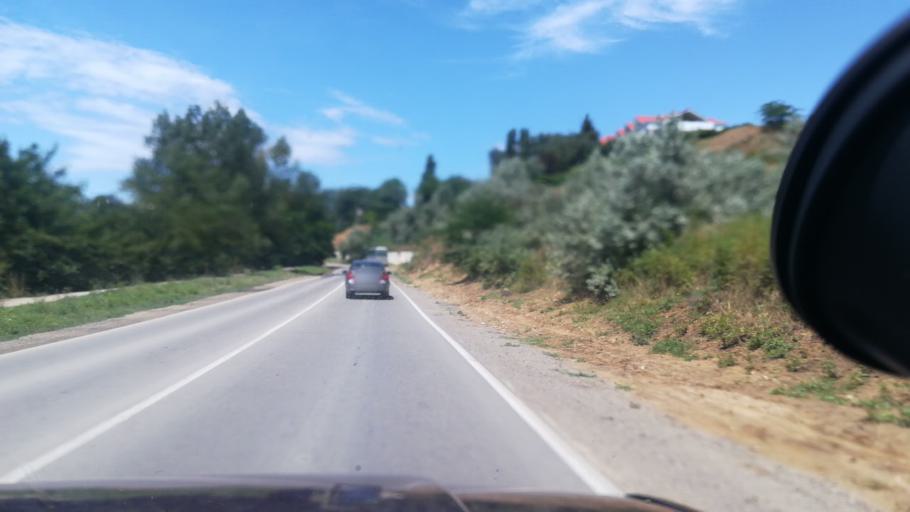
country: RU
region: Krasnodarskiy
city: Vityazevo
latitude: 44.9746
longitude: 37.2769
